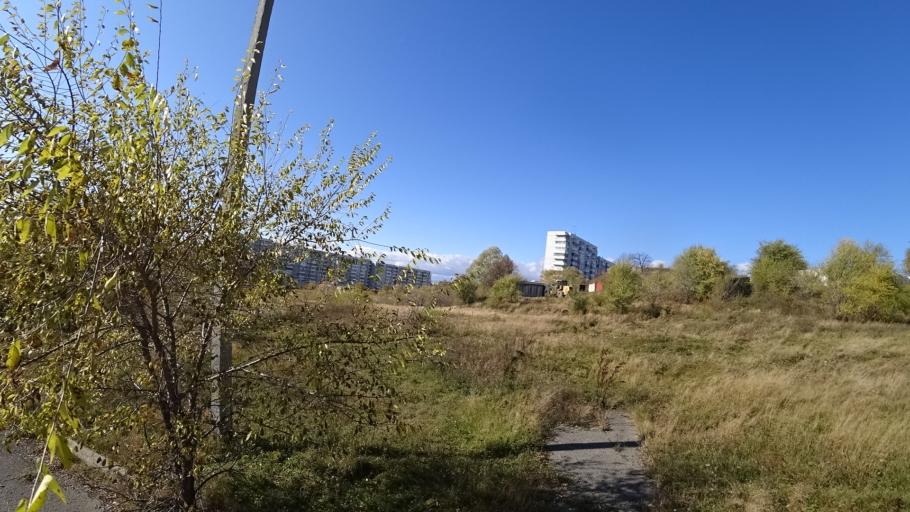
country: RU
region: Khabarovsk Krai
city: Amursk
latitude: 50.2393
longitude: 136.9180
